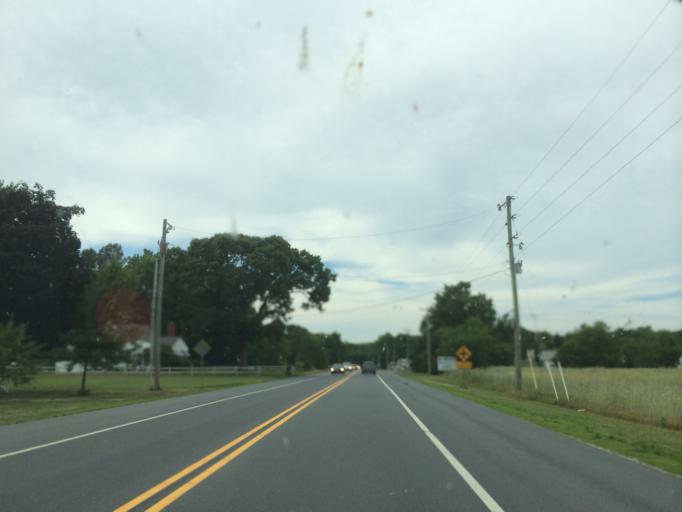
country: US
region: Delaware
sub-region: Sussex County
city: Bridgeville
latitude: 38.7909
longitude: -75.6890
